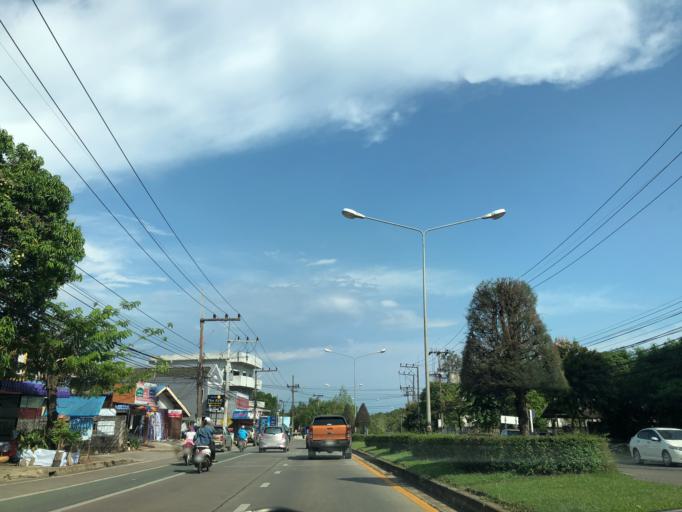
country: TH
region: Krabi
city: Krabi
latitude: 8.0755
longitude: 98.9162
